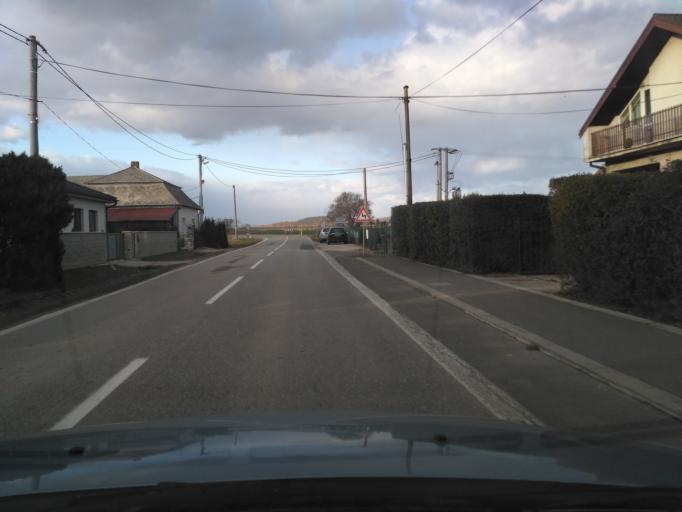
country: HU
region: Borsod-Abauj-Zemplen
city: Satoraljaujhely
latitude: 48.4106
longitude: 21.6678
